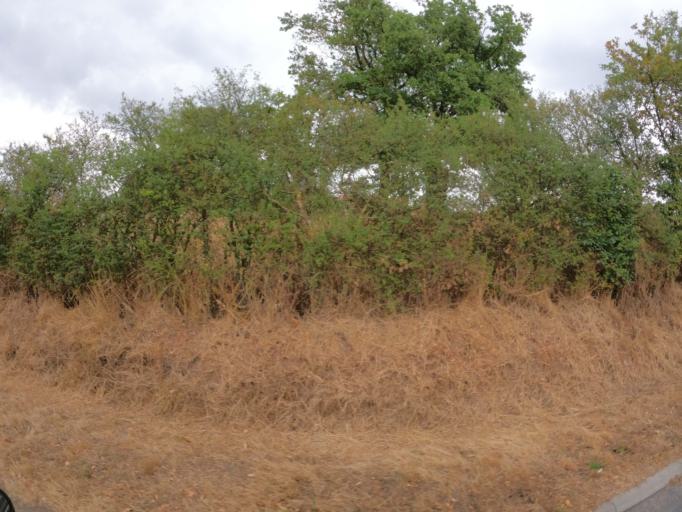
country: FR
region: Pays de la Loire
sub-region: Departement de Maine-et-Loire
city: Le Longeron
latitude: 46.9980
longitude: -1.0701
